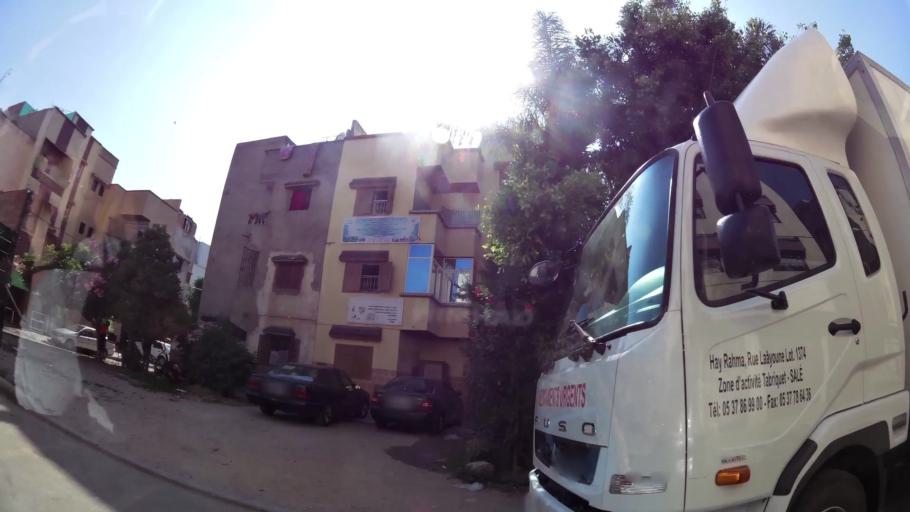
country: MA
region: Rabat-Sale-Zemmour-Zaer
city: Sale
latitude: 34.0430
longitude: -6.7770
